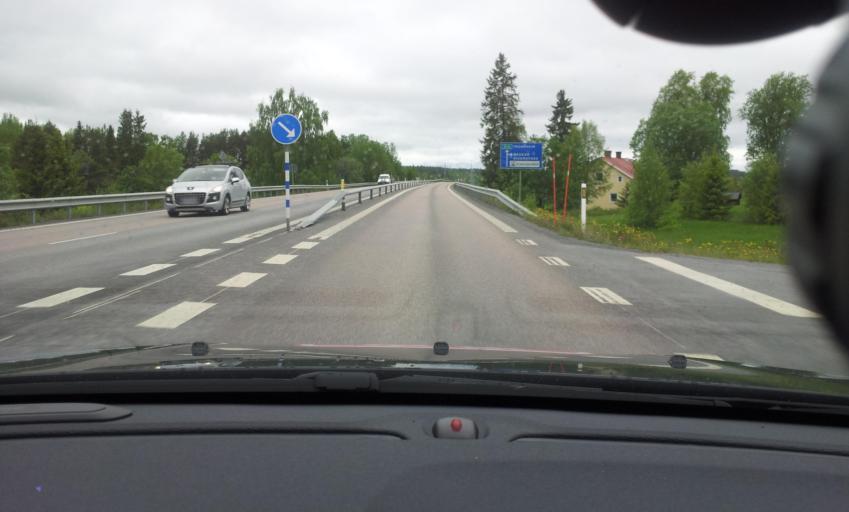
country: SE
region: Jaemtland
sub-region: Krokoms Kommun
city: Krokom
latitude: 63.3126
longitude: 14.4688
